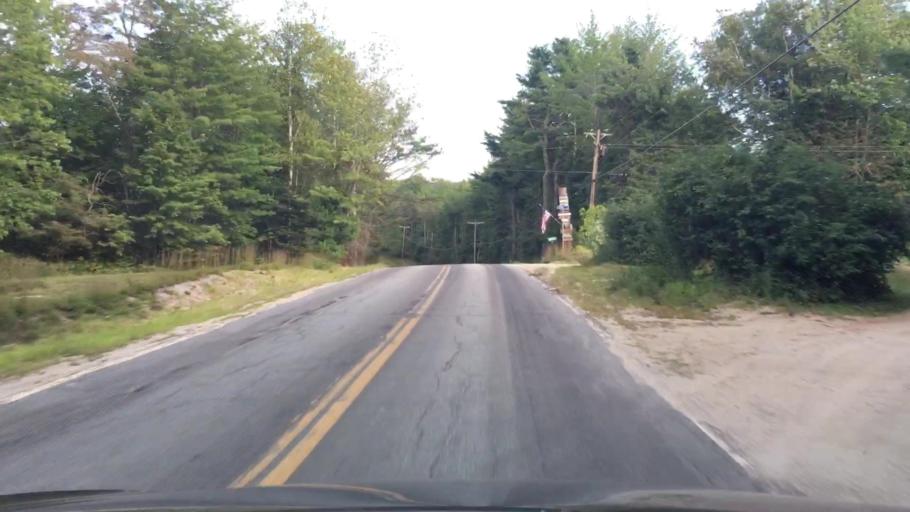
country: US
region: Maine
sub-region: Hancock County
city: Surry
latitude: 44.5067
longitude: -68.5945
